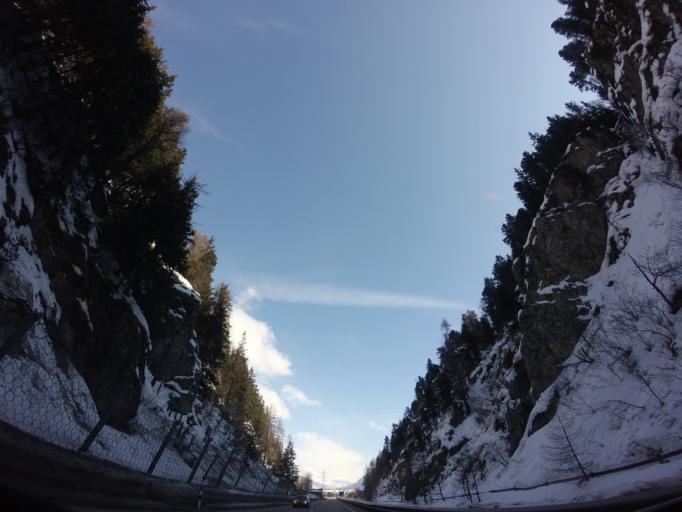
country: CH
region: Grisons
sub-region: Maloja District
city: Celerina
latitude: 46.5035
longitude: 9.8547
